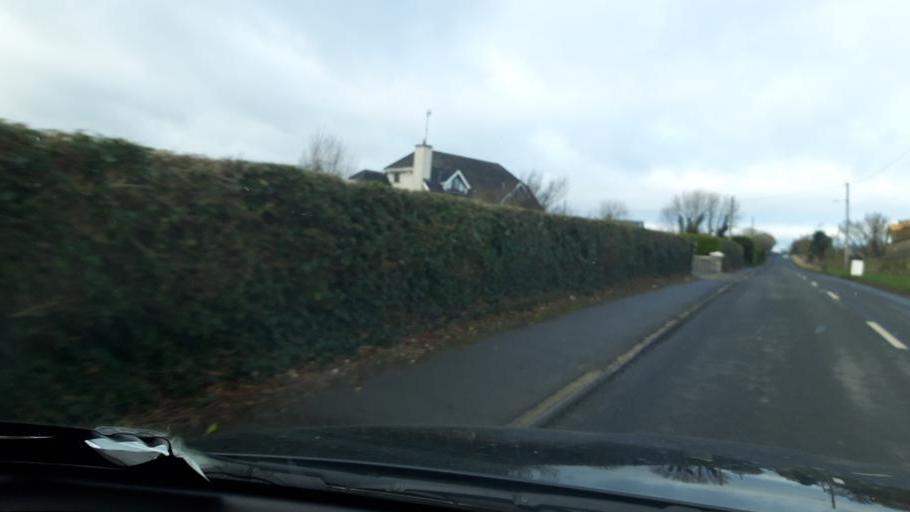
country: IE
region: Leinster
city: An Ros
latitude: 53.5424
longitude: -6.0963
